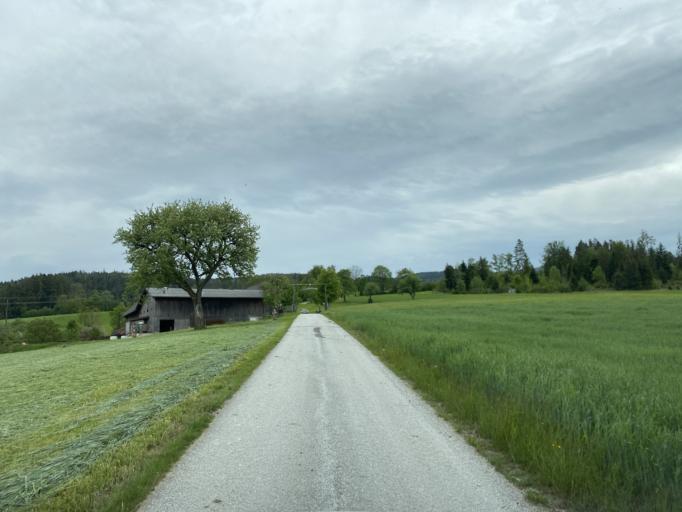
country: AT
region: Styria
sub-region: Politischer Bezirk Weiz
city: Gschaid bei Birkfeld
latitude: 47.3363
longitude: 15.7209
